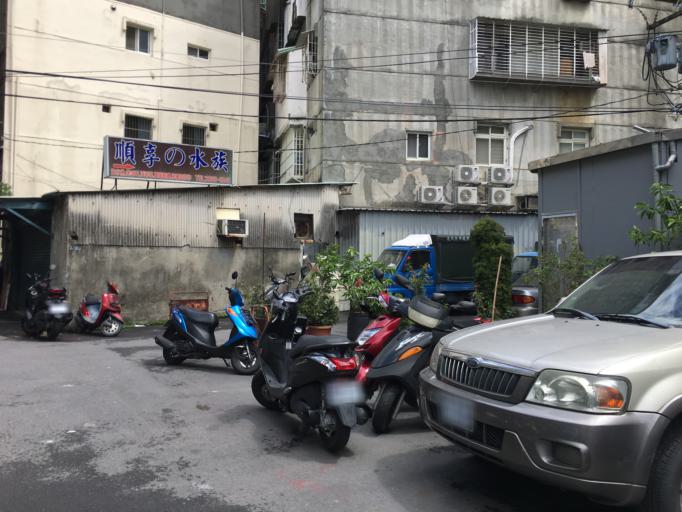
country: TW
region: Taipei
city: Taipei
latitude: 25.0877
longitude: 121.4781
